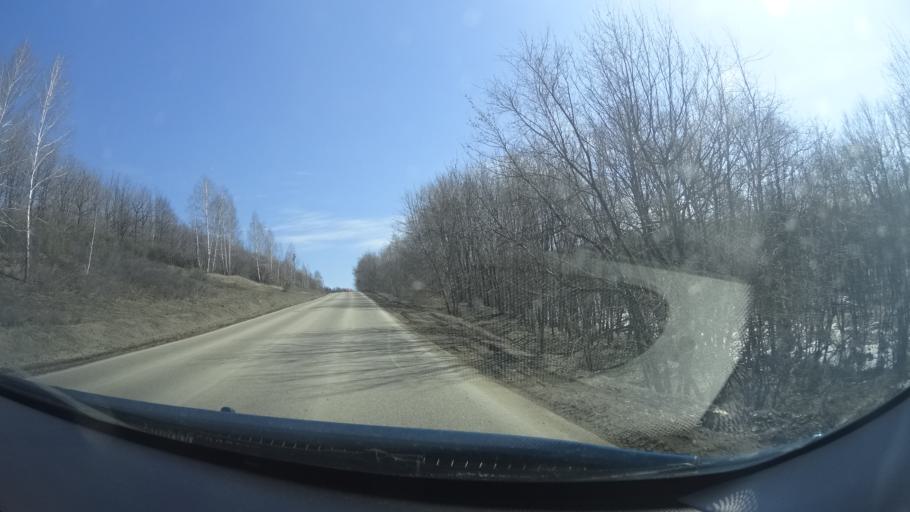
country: RU
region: Bashkortostan
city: Oktyabr'skiy
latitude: 54.4776
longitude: 53.5706
